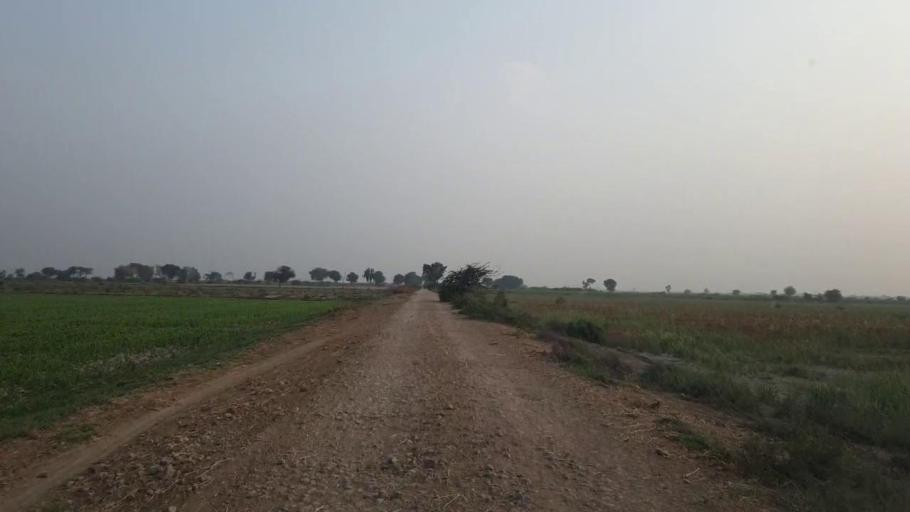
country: PK
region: Sindh
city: Mirpur Batoro
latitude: 24.6551
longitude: 68.3726
